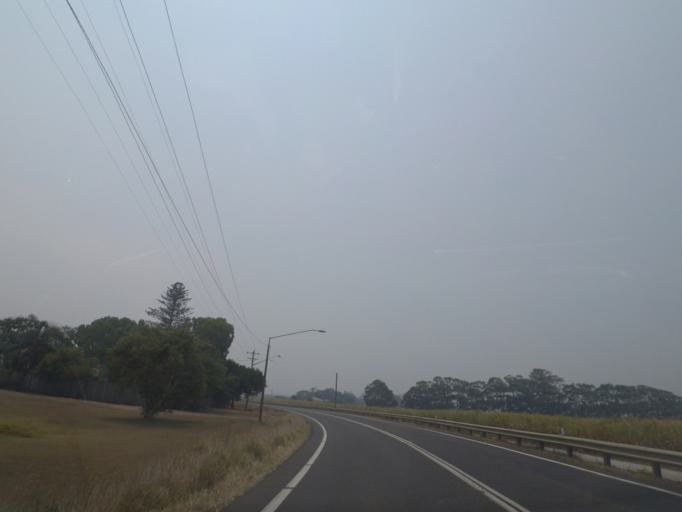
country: AU
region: New South Wales
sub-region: Richmond Valley
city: Evans Head
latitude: -29.0076
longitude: 153.4367
